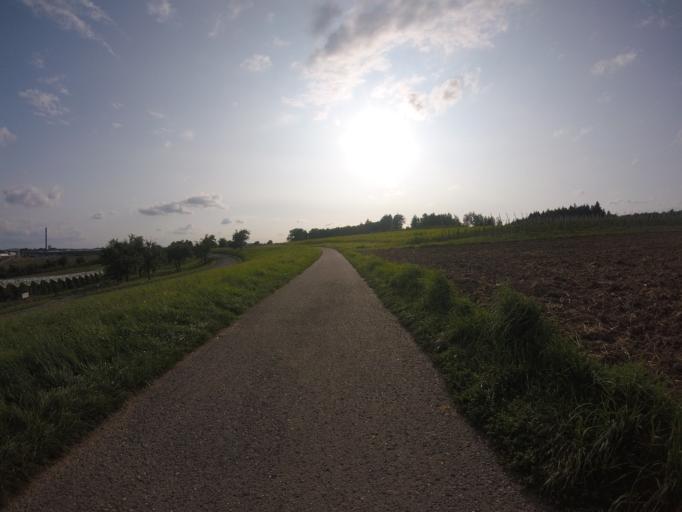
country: DE
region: Baden-Wuerttemberg
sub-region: Regierungsbezirk Stuttgart
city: Backnang
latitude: 48.9711
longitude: 9.4314
